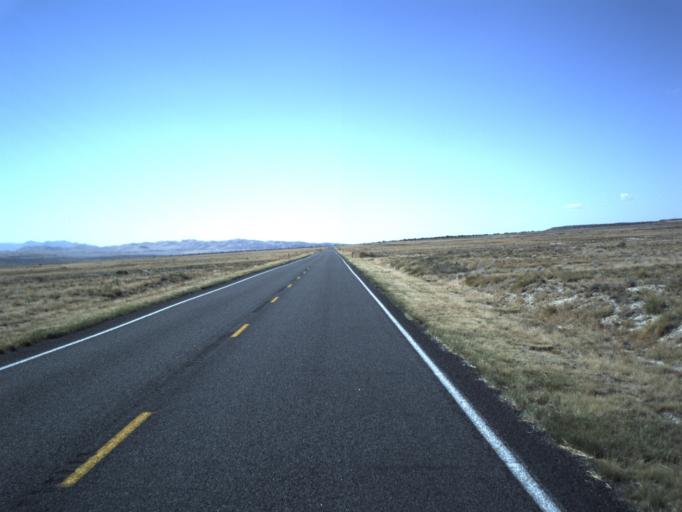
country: US
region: Utah
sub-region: Beaver County
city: Milford
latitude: 38.8667
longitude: -112.8368
